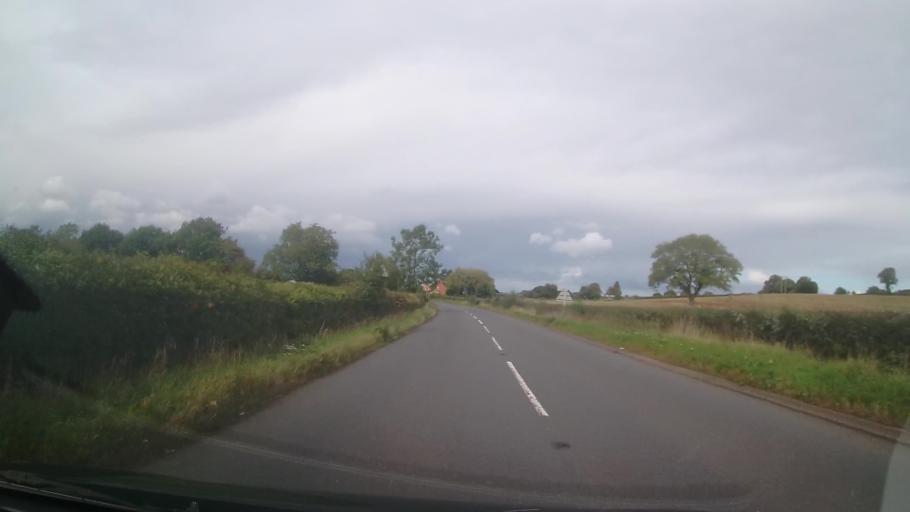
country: GB
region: England
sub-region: Shropshire
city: Romsley
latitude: 52.4445
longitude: -2.3338
